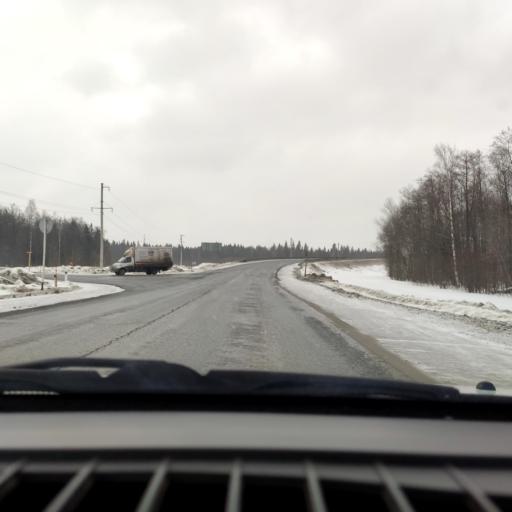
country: RU
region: Perm
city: Overyata
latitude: 58.1009
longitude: 55.8121
